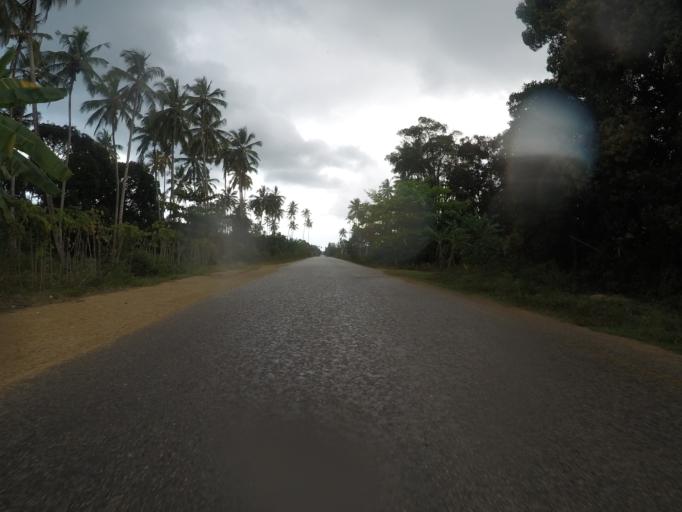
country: TZ
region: Zanzibar North
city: Mkokotoni
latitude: -5.9852
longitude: 39.1956
